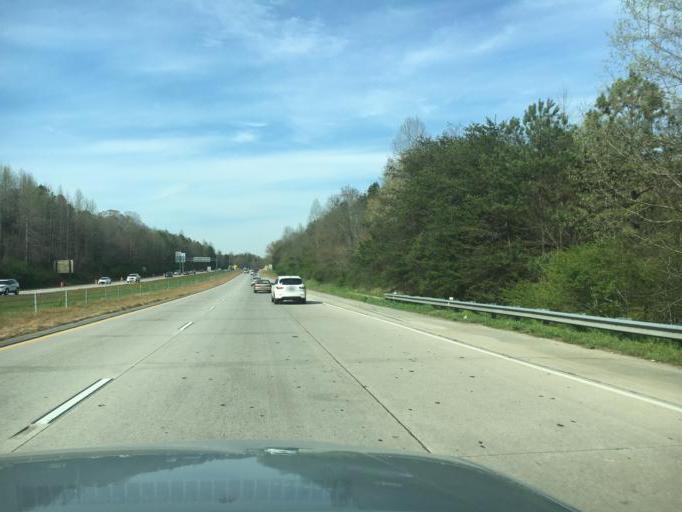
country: US
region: Georgia
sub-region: Hall County
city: Gainesville
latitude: 34.3226
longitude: -83.7876
